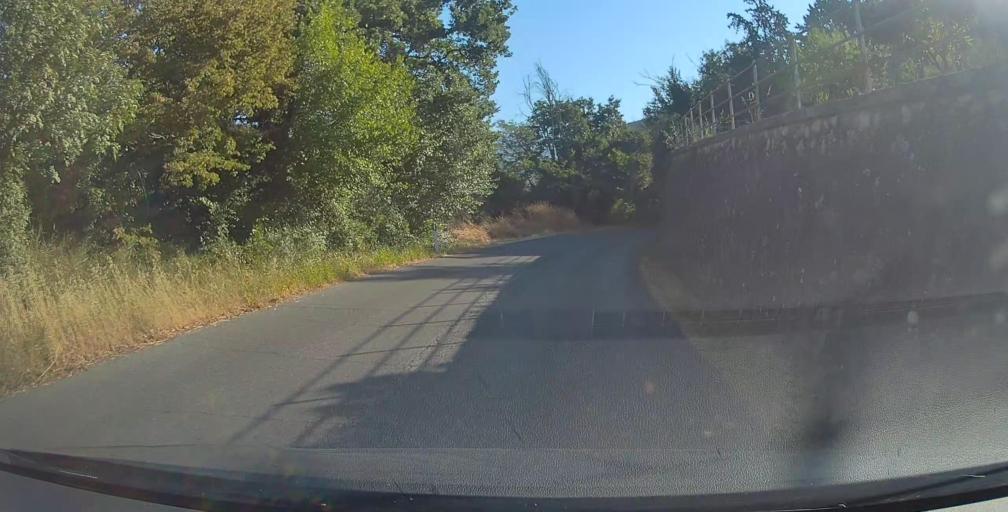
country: IT
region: Umbria
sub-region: Provincia di Terni
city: Calvi dell'Umbria
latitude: 42.3963
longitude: 12.5684
